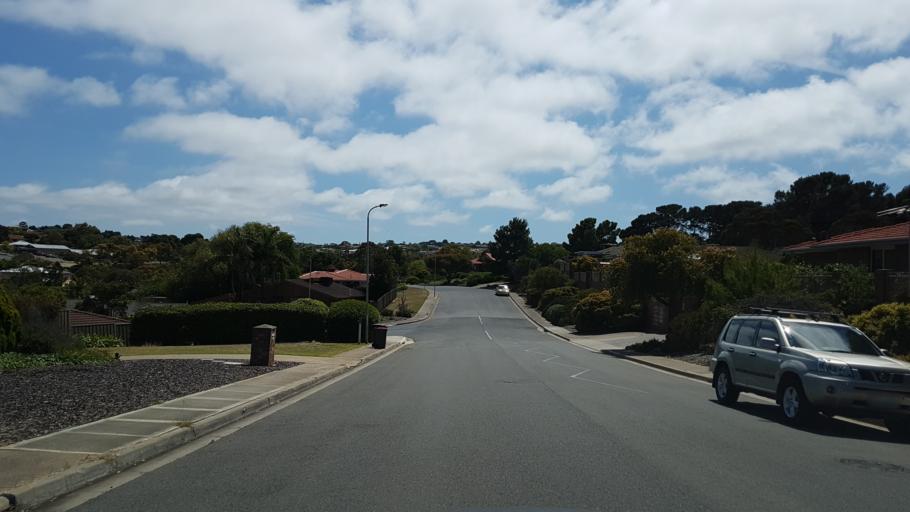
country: AU
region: South Australia
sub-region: Marion
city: Happy Valley
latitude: -35.0754
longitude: 138.5175
